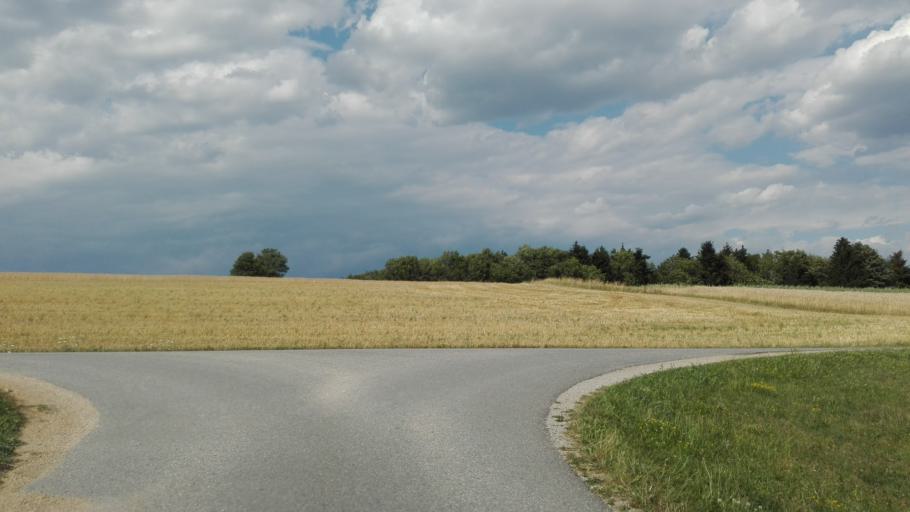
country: AT
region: Upper Austria
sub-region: Politischer Bezirk Perg
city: Bad Kreuzen
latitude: 48.2521
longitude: 14.7220
